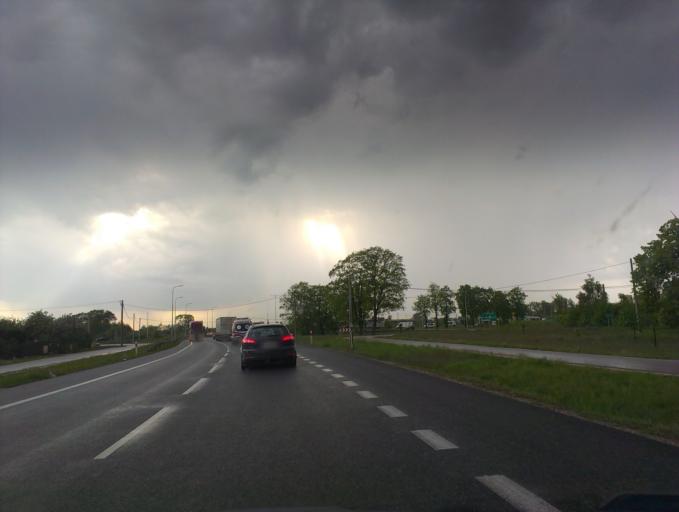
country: PL
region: Masovian Voivodeship
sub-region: Powiat zyrardowski
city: Mszczonow
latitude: 51.9811
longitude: 20.5302
